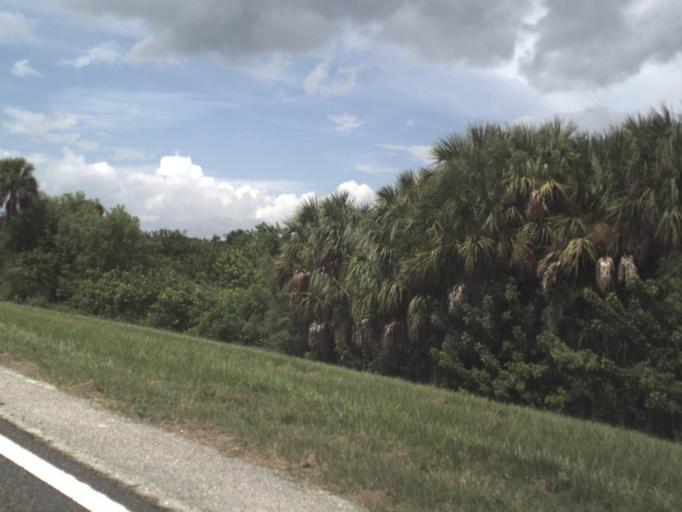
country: US
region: Florida
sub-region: Manatee County
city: Memphis
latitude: 27.5838
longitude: -82.5814
